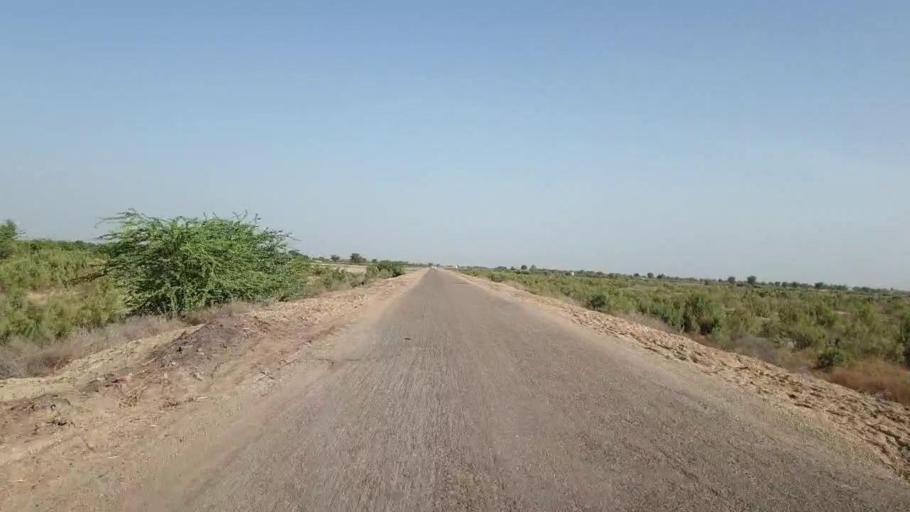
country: PK
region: Sindh
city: Nawabshah
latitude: 26.1531
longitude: 68.4469
